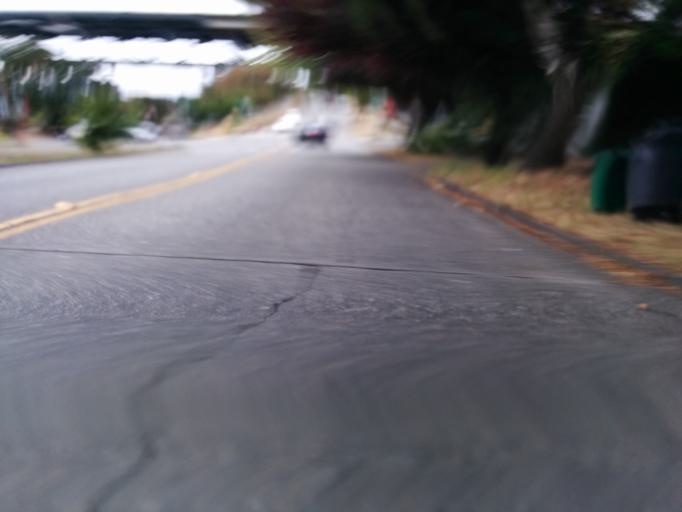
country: US
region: Washington
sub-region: King County
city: Seattle
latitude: 47.6559
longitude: -122.3201
